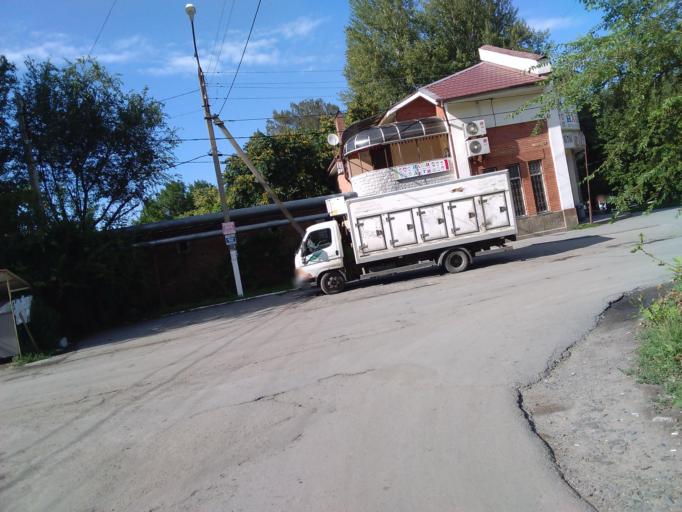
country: RU
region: Rostov
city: Bataysk
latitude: 47.1292
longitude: 39.7364
